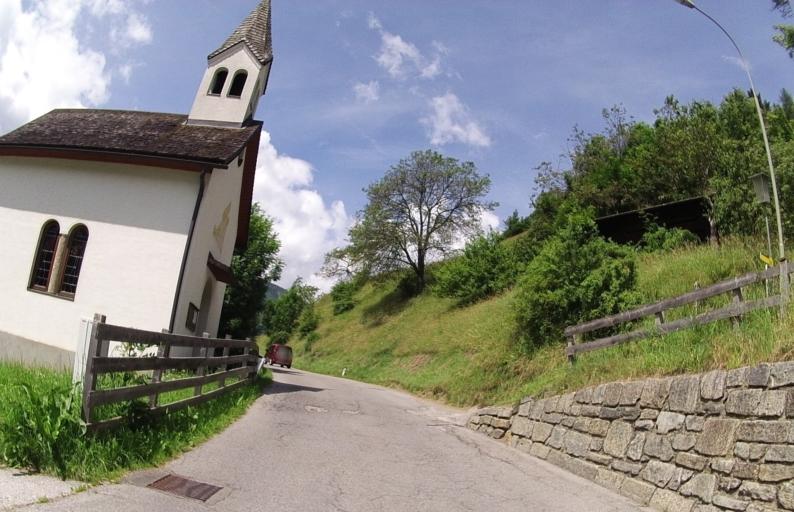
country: AT
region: Tyrol
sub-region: Politischer Bezirk Innsbruck Land
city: Ellbogen
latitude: 47.1631
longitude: 11.4569
